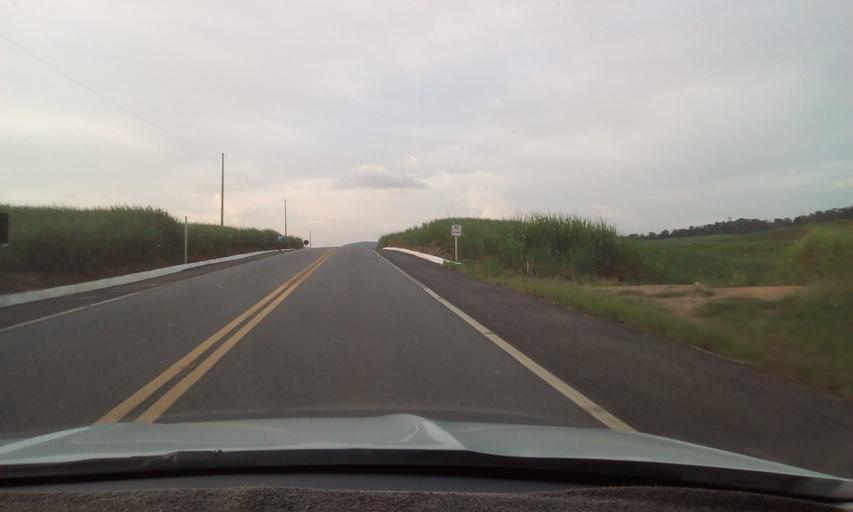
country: BR
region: Pernambuco
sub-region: Vicencia
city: Vicencia
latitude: -7.6514
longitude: -35.2514
